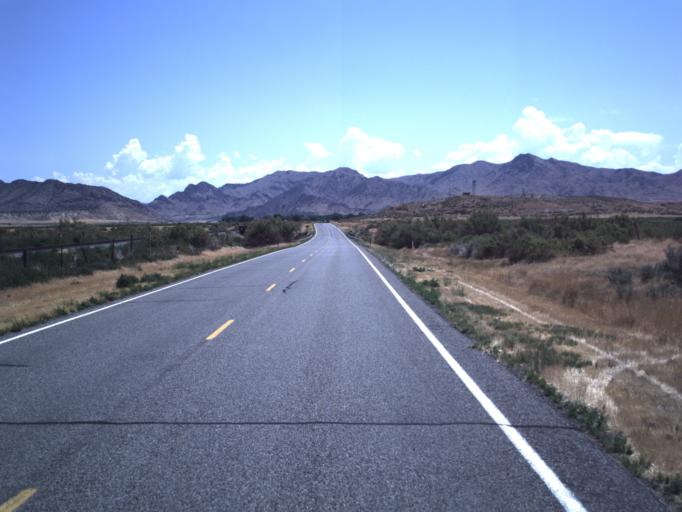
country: US
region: Utah
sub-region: Millard County
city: Delta
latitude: 39.5331
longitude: -112.3246
